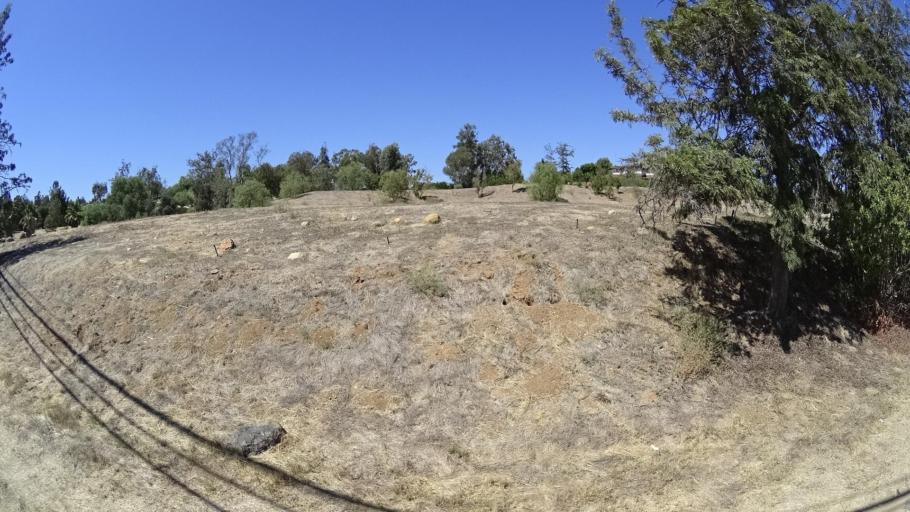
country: US
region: California
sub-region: San Diego County
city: Rancho Santa Fe
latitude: 33.0341
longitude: -117.1848
